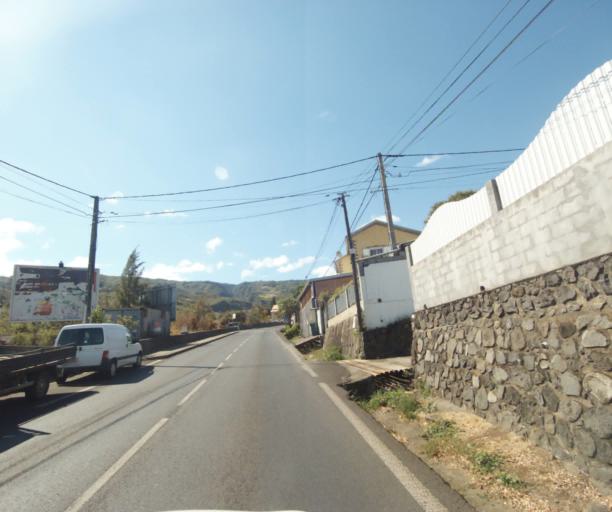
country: RE
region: Reunion
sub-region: Reunion
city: La Possession
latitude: -20.9809
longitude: 55.3334
